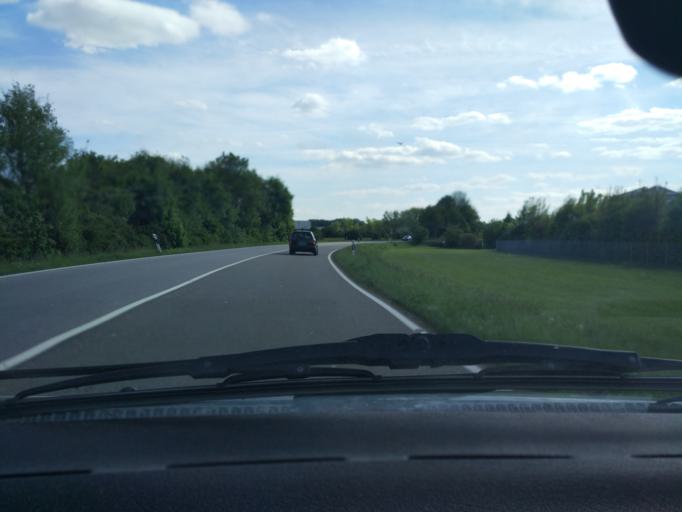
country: DE
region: Rheinland-Pfalz
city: Grolsheim
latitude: 49.9084
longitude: 7.9216
